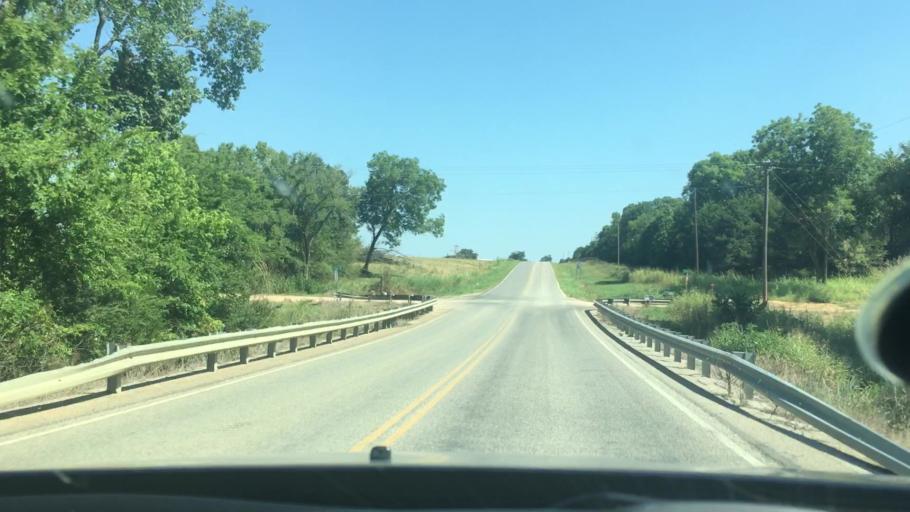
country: US
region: Oklahoma
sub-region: Johnston County
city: Tishomingo
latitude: 34.2736
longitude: -96.6186
